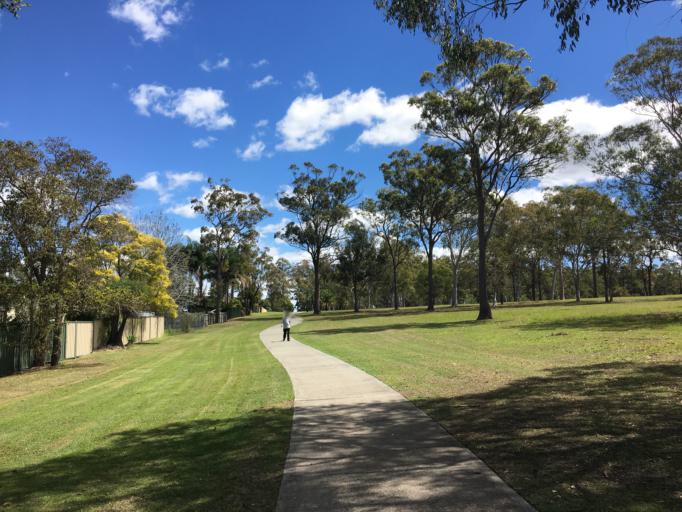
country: AU
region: Queensland
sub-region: Logan
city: Logan City
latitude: -27.6489
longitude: 153.1052
